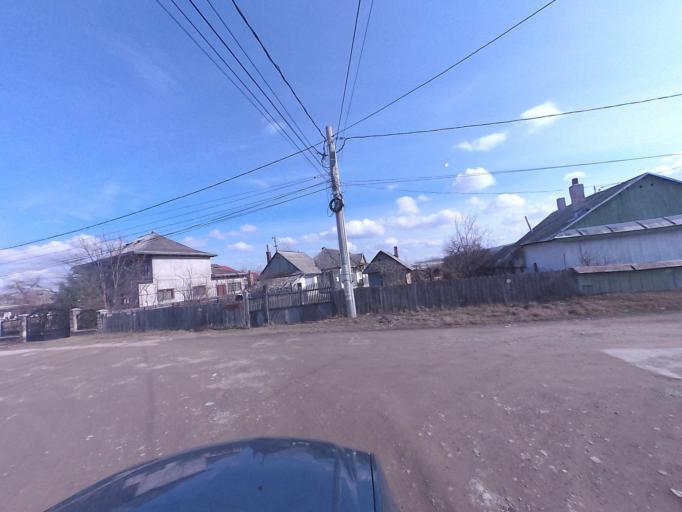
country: RO
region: Neamt
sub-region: Oras Targu Neamt
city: Targu Neamt
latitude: 47.2054
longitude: 26.3836
